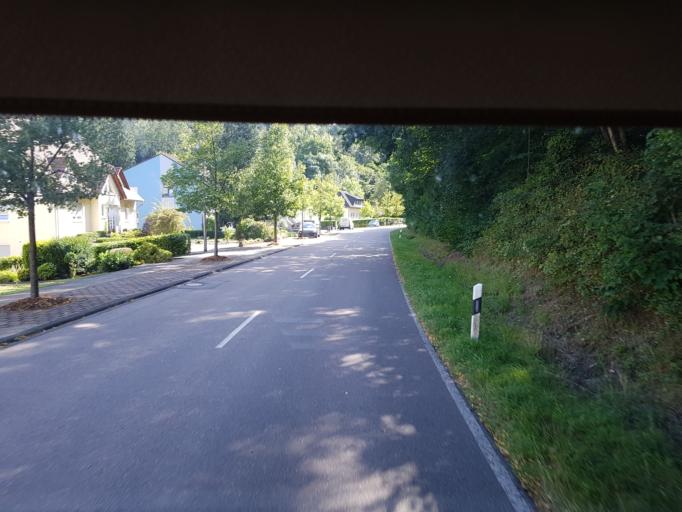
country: DE
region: Rheinland-Pfalz
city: Kanzem
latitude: 49.6763
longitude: 6.5508
